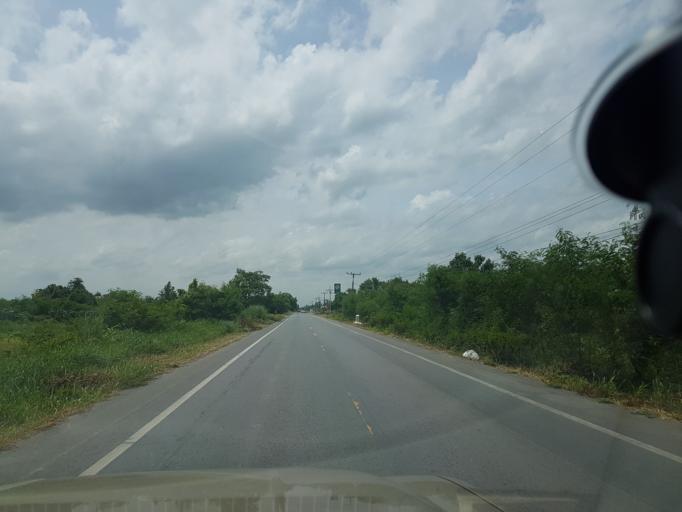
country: TH
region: Sara Buri
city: Nong Khae
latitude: 14.2660
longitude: 100.8918
